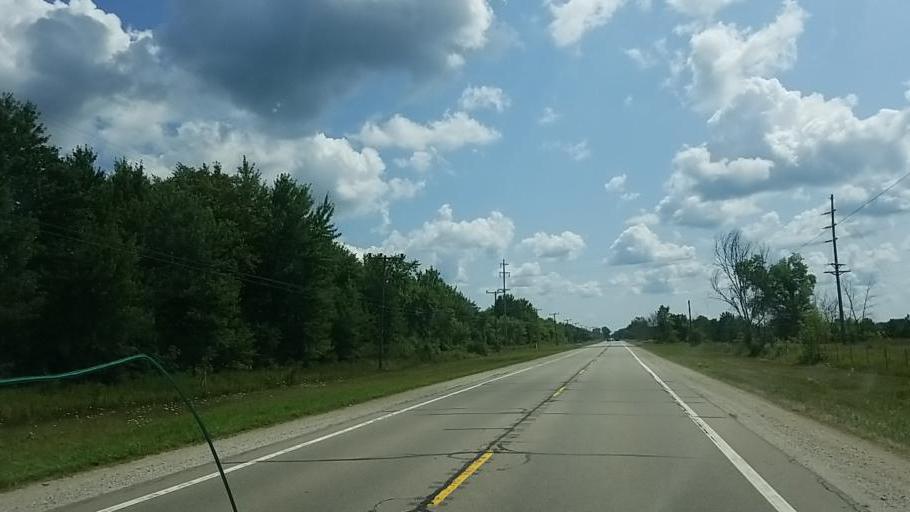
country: US
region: Michigan
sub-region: Muskegon County
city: Ravenna
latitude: 43.2350
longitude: -85.9963
